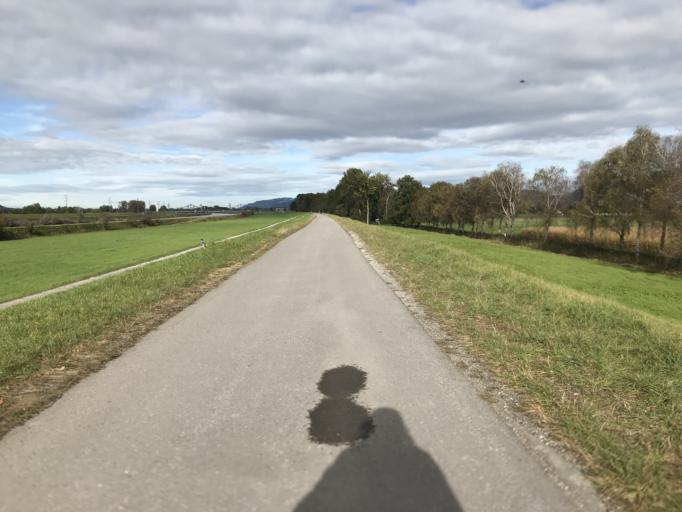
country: CH
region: Saint Gallen
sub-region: Wahlkreis Rheintal
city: Diepoldsau
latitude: 47.3741
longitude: 9.6360
